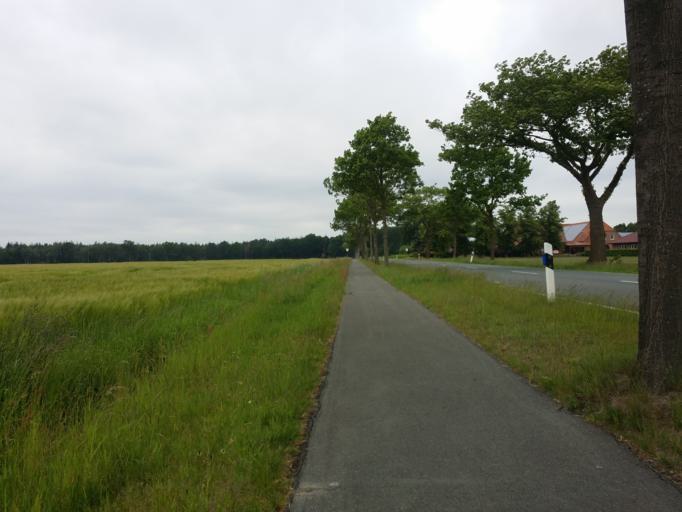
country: DE
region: Lower Saxony
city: Hatten
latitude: 53.0696
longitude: 8.4237
